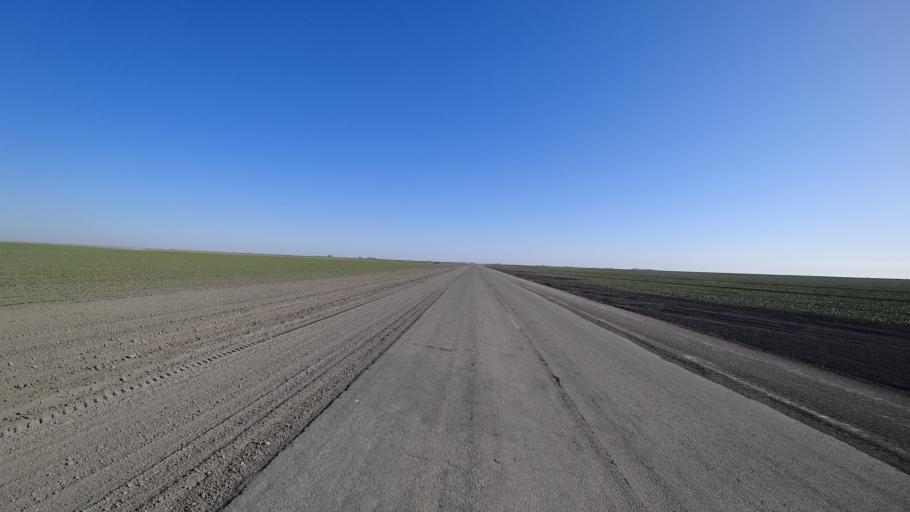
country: US
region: California
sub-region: Kings County
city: Stratford
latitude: 36.1122
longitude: -119.7981
